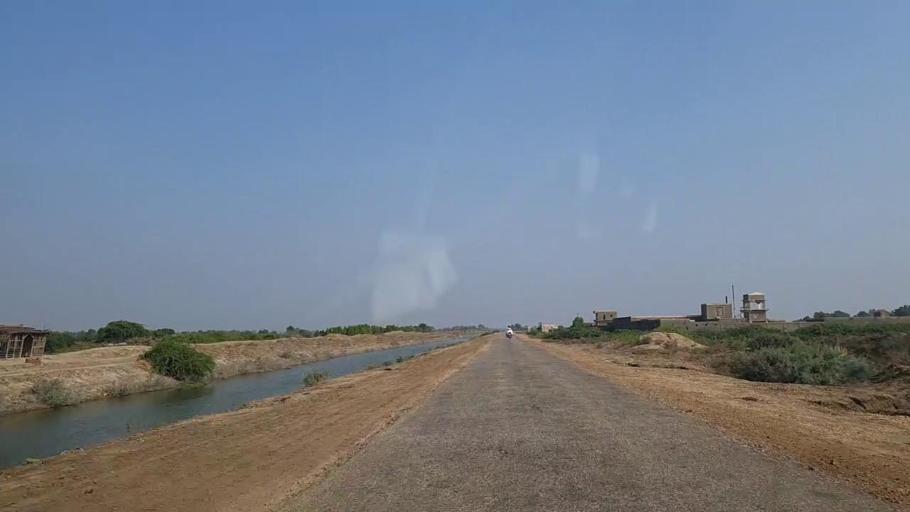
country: PK
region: Sindh
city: Mirpur Sakro
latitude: 24.6351
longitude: 67.6086
